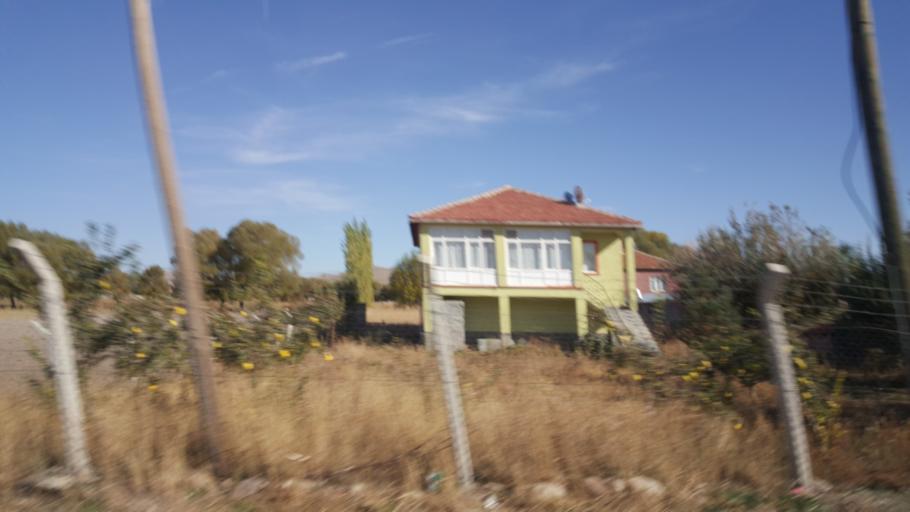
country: TR
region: Ankara
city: Altpinar
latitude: 39.2608
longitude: 32.7524
